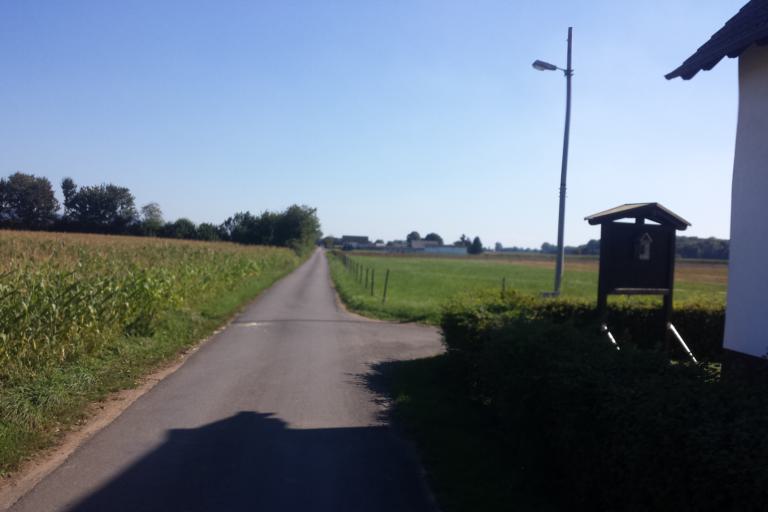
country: DE
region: Hesse
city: Viernheim
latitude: 49.5750
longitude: 8.5959
